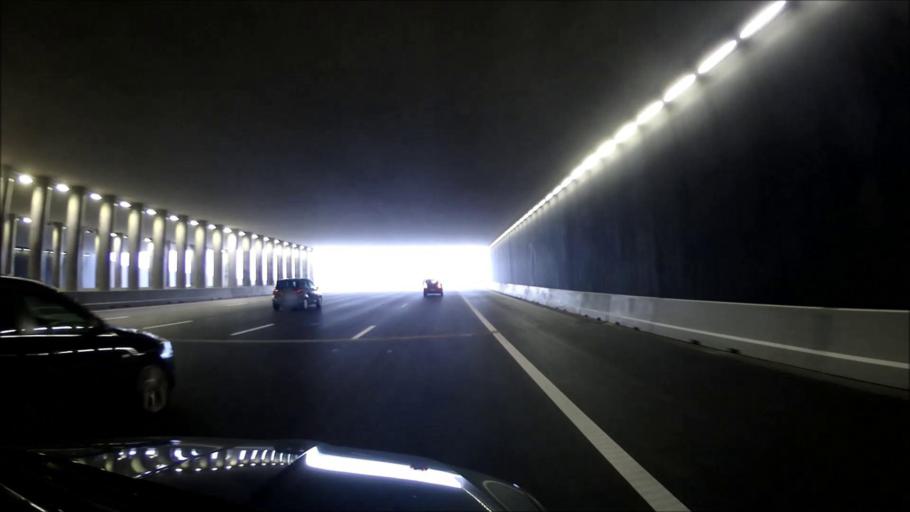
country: NL
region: North Holland
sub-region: Gemeente Weesp
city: Weesp
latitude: 52.3244
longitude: 5.0625
